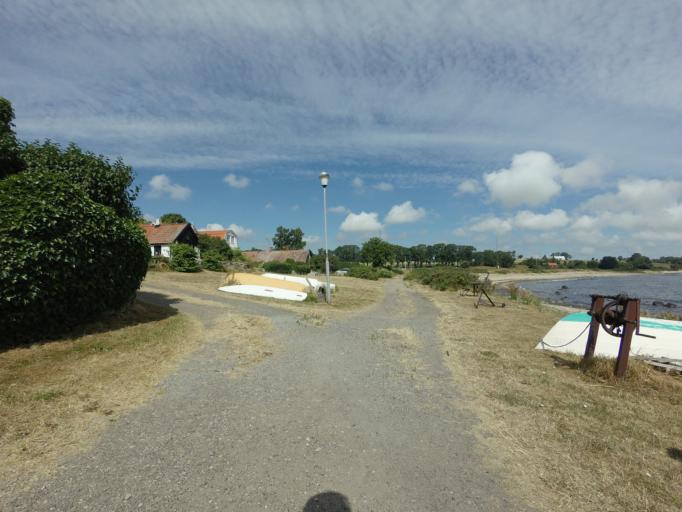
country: SE
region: Skane
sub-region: Simrishamns Kommun
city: Simrishamn
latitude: 55.4874
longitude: 14.3166
